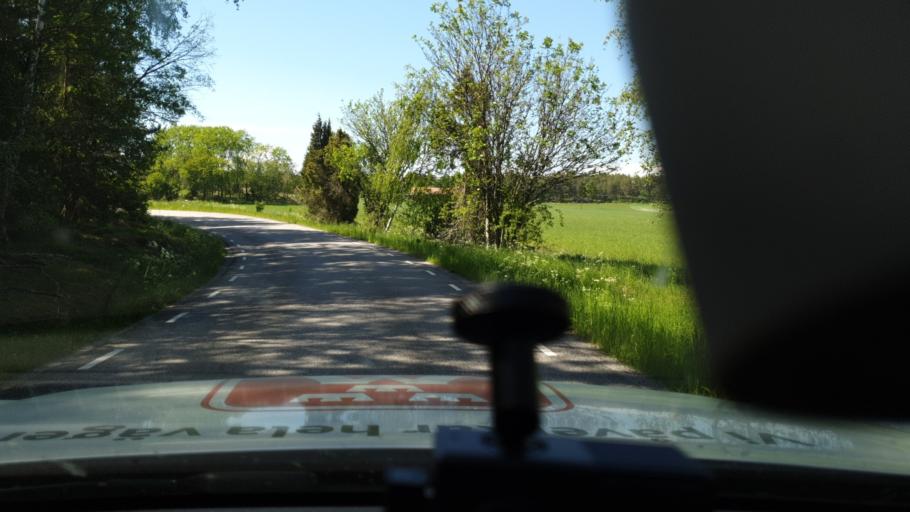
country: SE
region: Kalmar
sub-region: Vasterviks Kommun
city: Vaestervik
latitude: 57.9291
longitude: 16.7315
